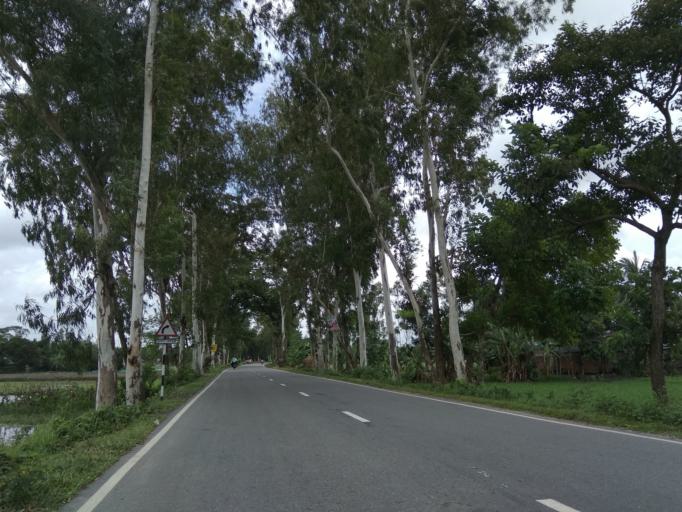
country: BD
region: Rajshahi
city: Saidpur
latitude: 25.7698
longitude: 88.8064
